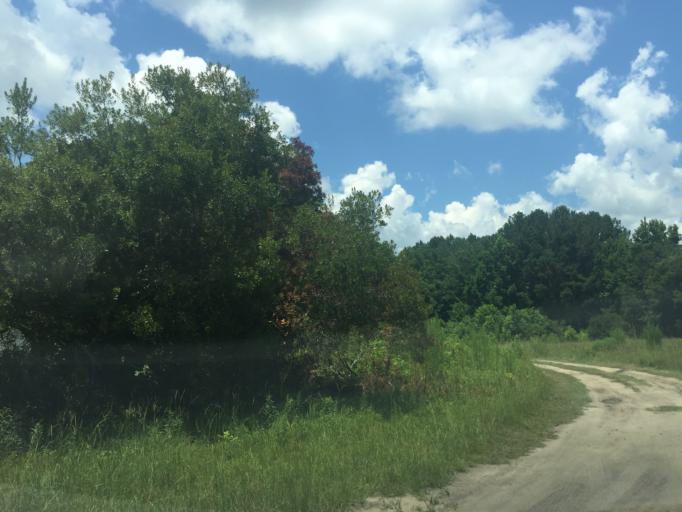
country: US
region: South Carolina
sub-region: Jasper County
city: Ridgeland
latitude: 32.4785
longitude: -80.9610
